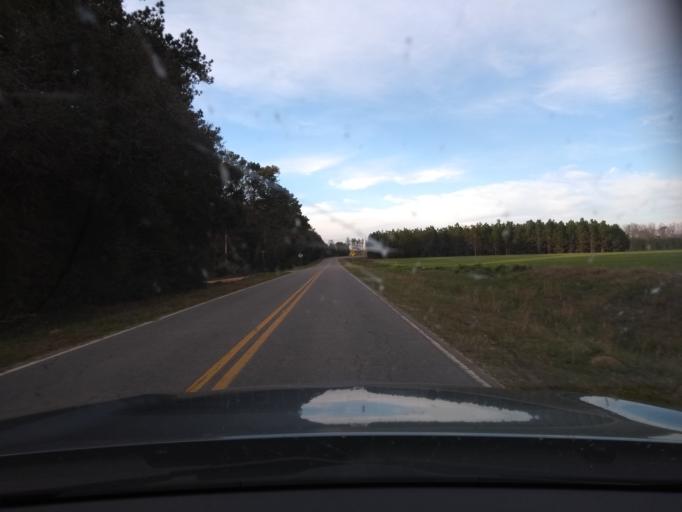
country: US
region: Georgia
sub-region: Evans County
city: Claxton
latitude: 32.2478
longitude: -81.7695
